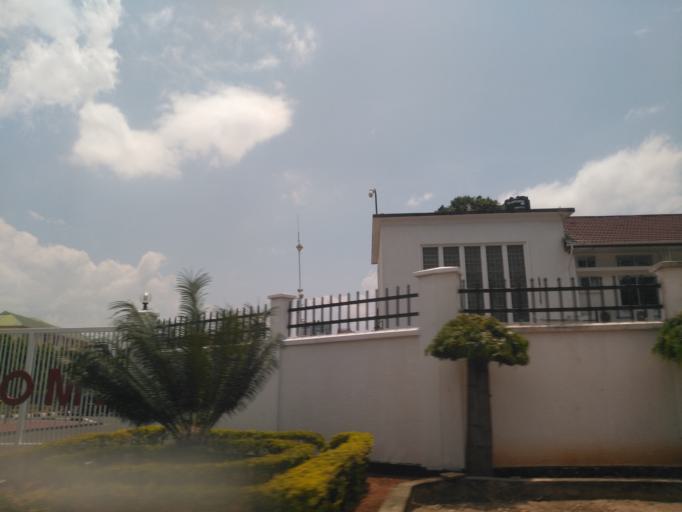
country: TZ
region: Dar es Salaam
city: Dar es Salaam
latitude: -6.8032
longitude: 39.2811
